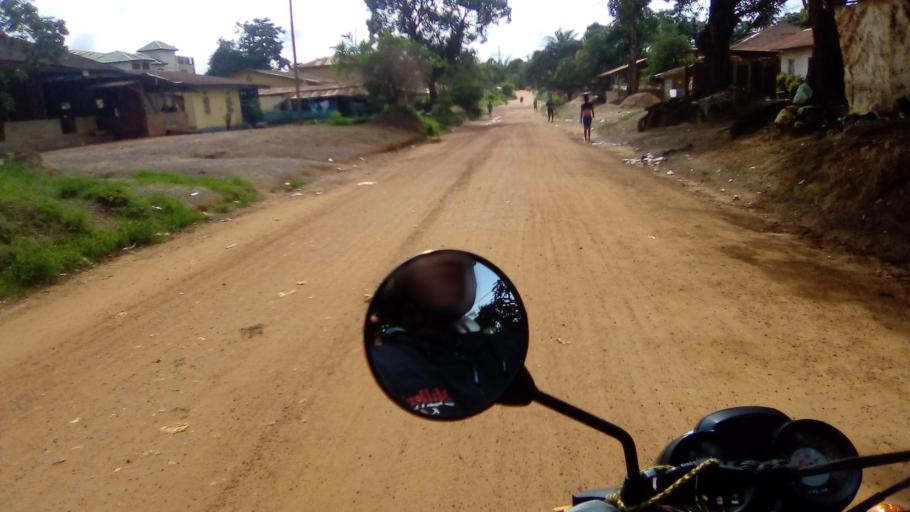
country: SL
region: Southern Province
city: Bo
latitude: 7.9577
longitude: -11.7528
